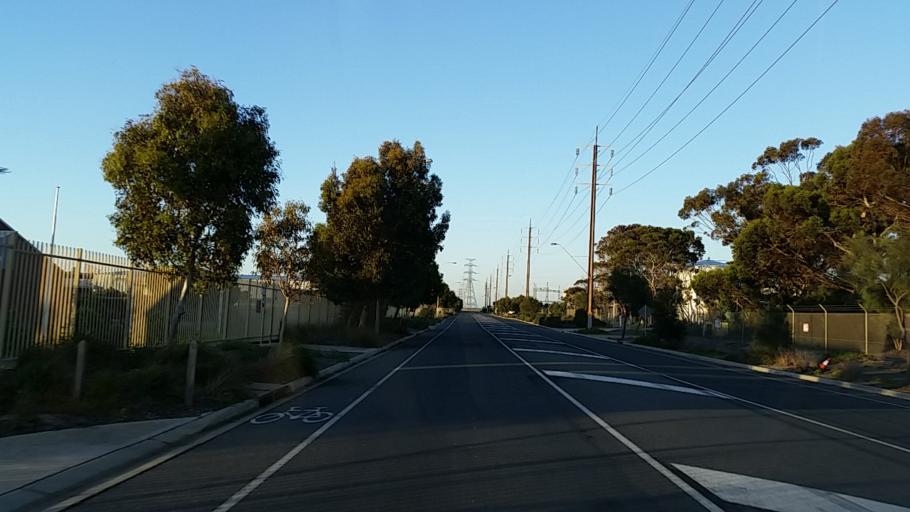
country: AU
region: South Australia
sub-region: Port Adelaide Enfield
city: Birkenhead
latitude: -34.7842
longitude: 138.5074
